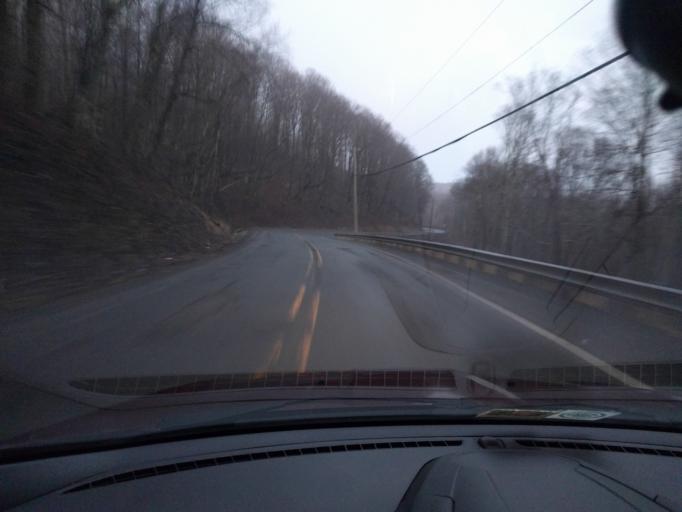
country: US
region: West Virginia
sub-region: Greenbrier County
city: Rainelle
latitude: 37.9855
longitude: -80.8493
